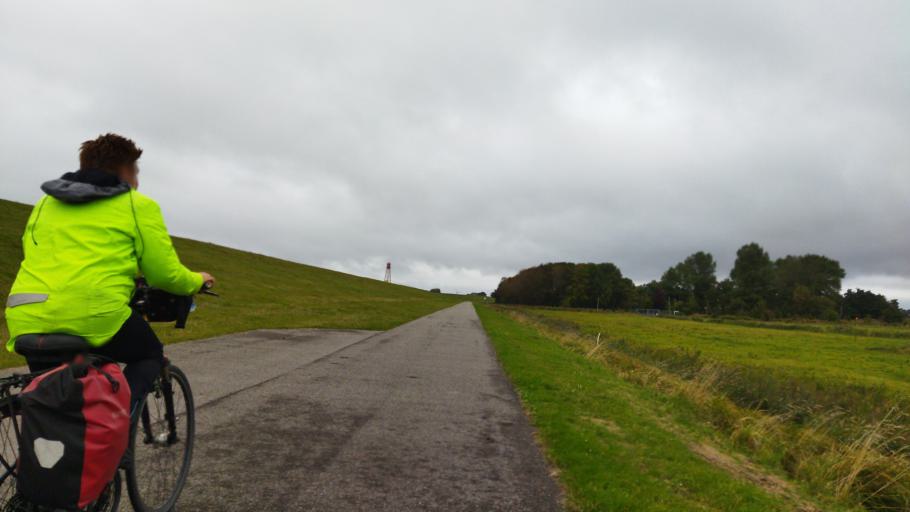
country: NL
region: Groningen
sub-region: Gemeente Delfzijl
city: Delfzijl
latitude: 53.3948
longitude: 7.0126
